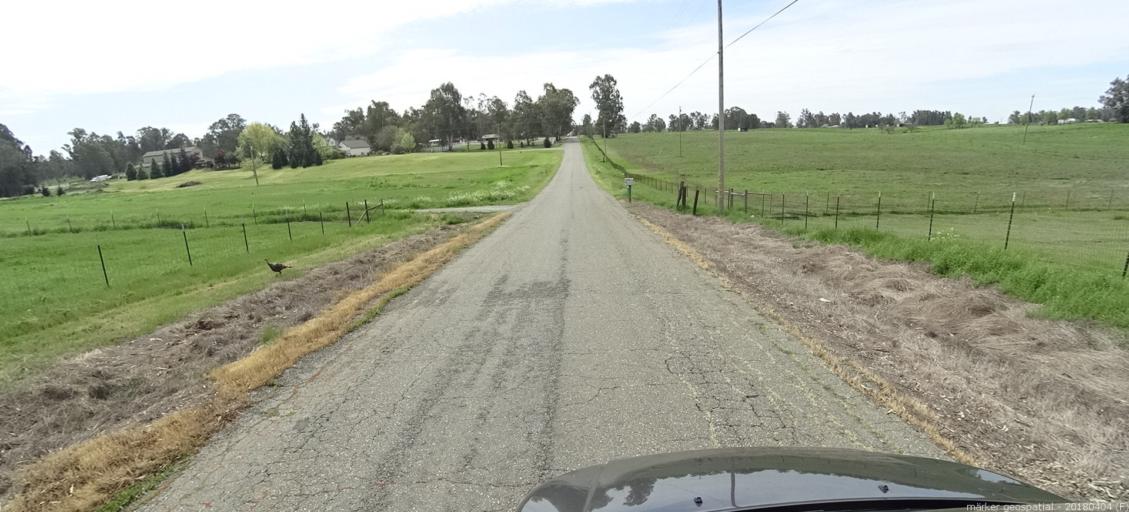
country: US
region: California
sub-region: Sacramento County
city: Clay
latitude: 38.3300
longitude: -121.1499
